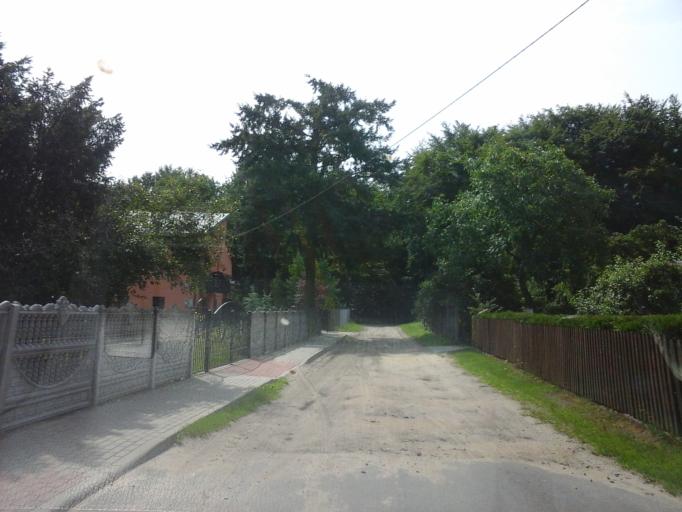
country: PL
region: West Pomeranian Voivodeship
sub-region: Powiat choszczenski
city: Bierzwnik
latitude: 53.0298
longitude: 15.6655
